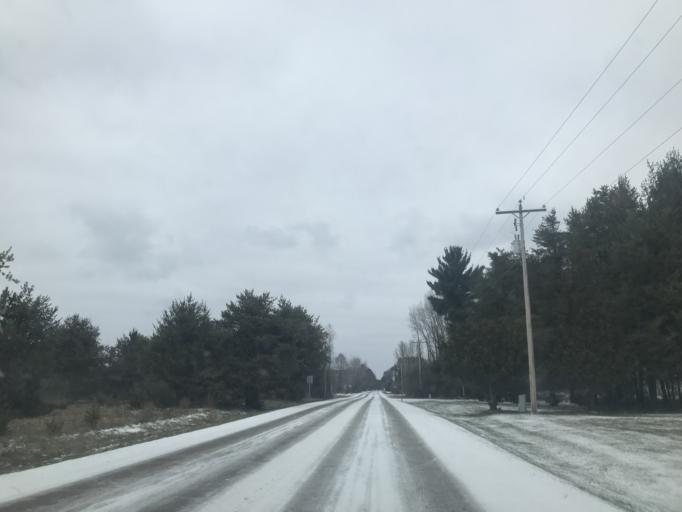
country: US
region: Wisconsin
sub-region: Marinette County
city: Marinette
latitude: 45.0553
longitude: -87.6582
